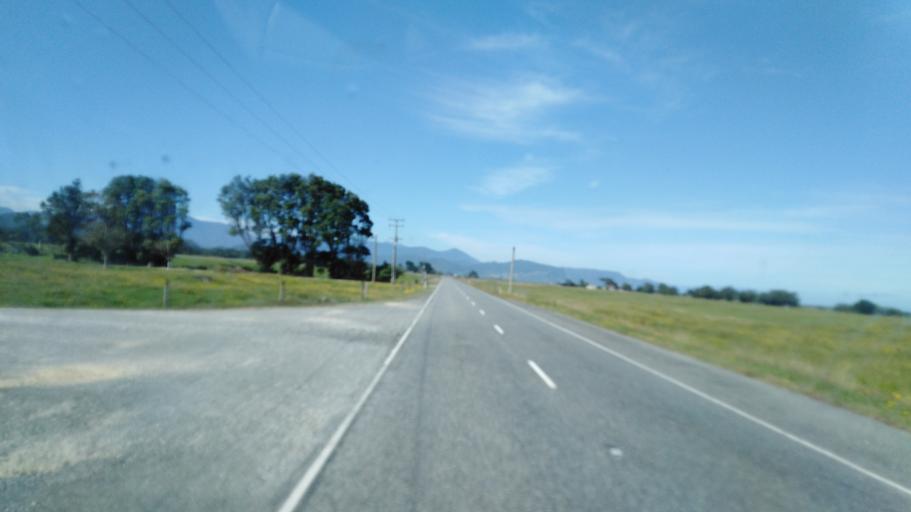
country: NZ
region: West Coast
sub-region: Buller District
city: Westport
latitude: -41.3063
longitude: 172.0919
